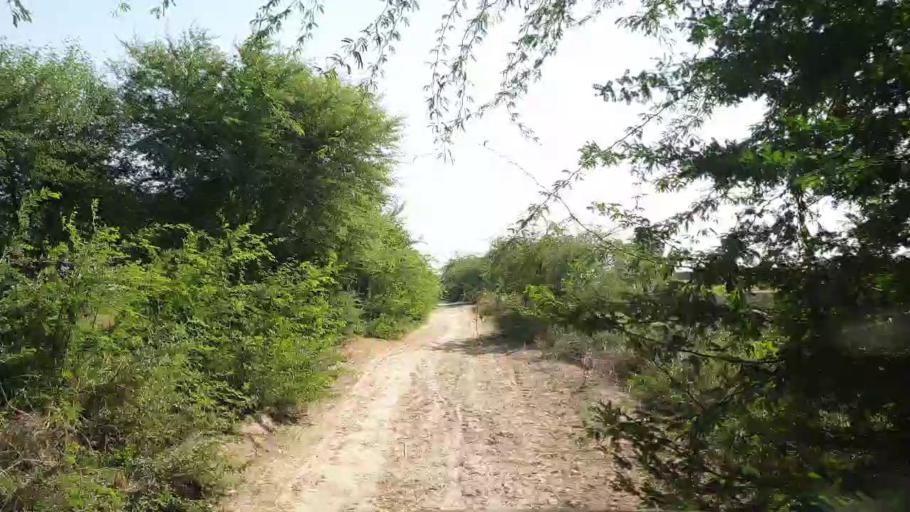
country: PK
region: Sindh
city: Kadhan
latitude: 24.5931
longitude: 69.0069
